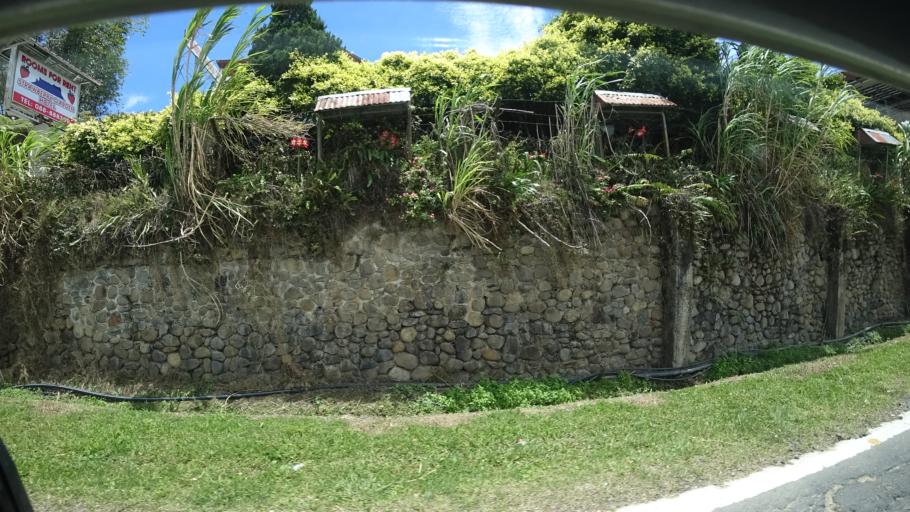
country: MY
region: Sabah
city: Ranau
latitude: 5.9817
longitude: 116.5595
